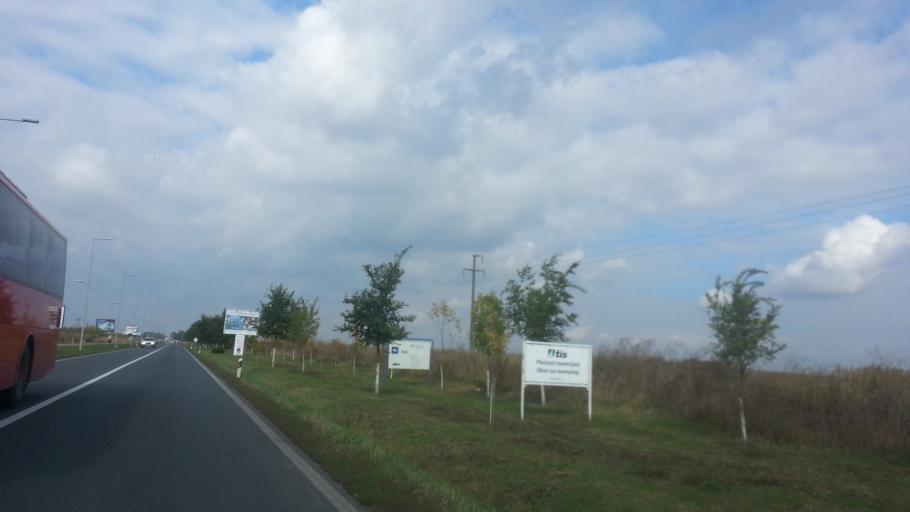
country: RS
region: Autonomna Pokrajina Vojvodina
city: Nova Pazova
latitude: 44.9578
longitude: 20.1990
